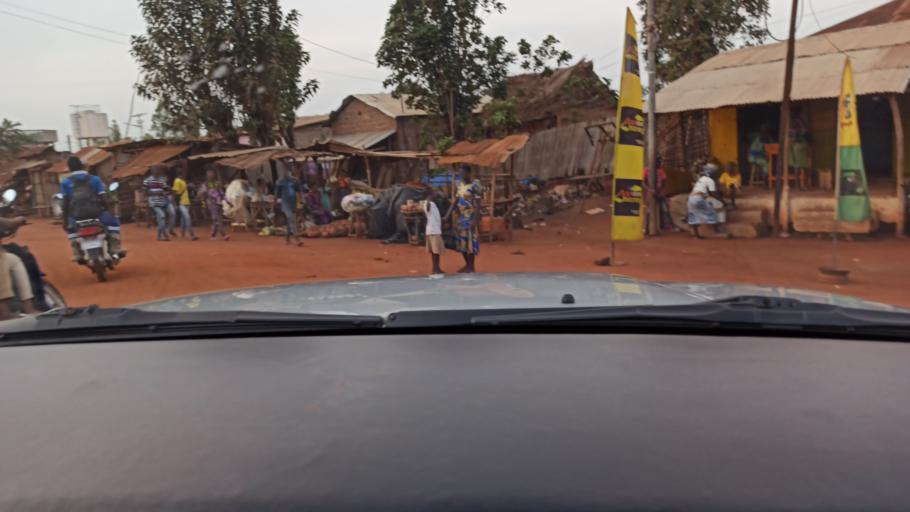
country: BJ
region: Queme
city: Porto-Novo
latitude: 6.5323
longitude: 2.6631
